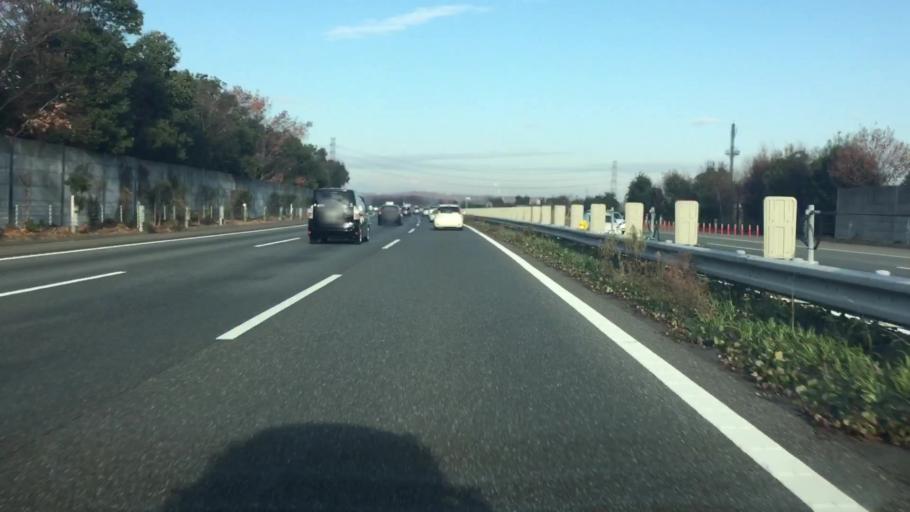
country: JP
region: Saitama
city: Honjo
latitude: 36.1962
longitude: 139.1864
